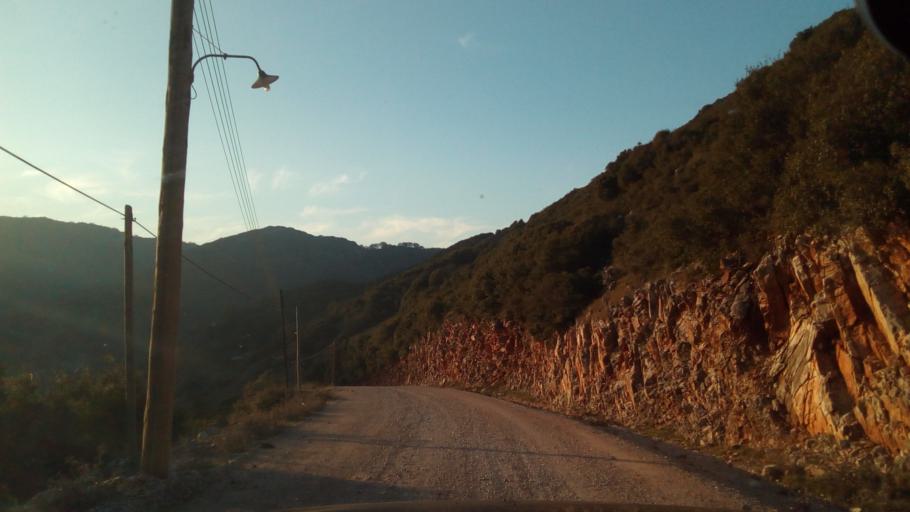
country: GR
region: West Greece
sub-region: Nomos Aitolias kai Akarnanias
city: Nafpaktos
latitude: 38.4688
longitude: 21.8209
